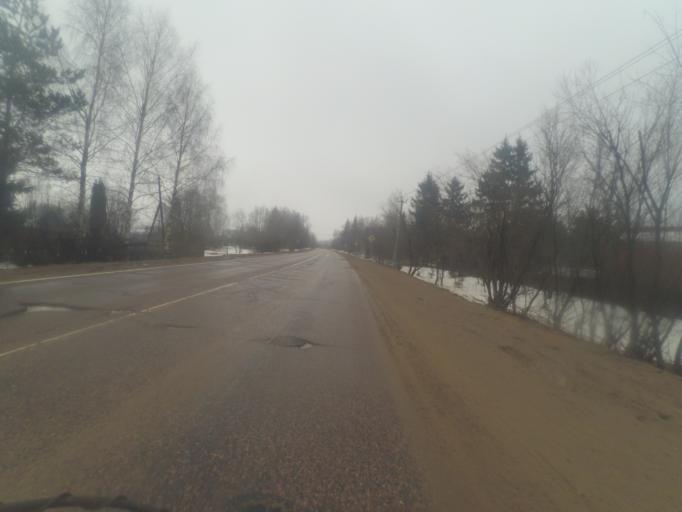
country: RU
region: Moskovskaya
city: Avtopoligon
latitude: 56.2645
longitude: 37.2154
